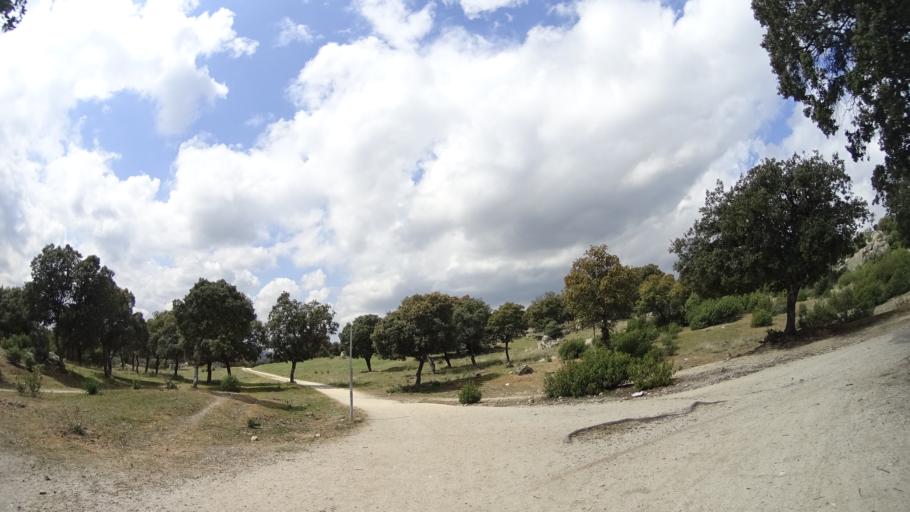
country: ES
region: Madrid
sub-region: Provincia de Madrid
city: Hoyo de Manzanares
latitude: 40.6194
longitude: -3.8906
